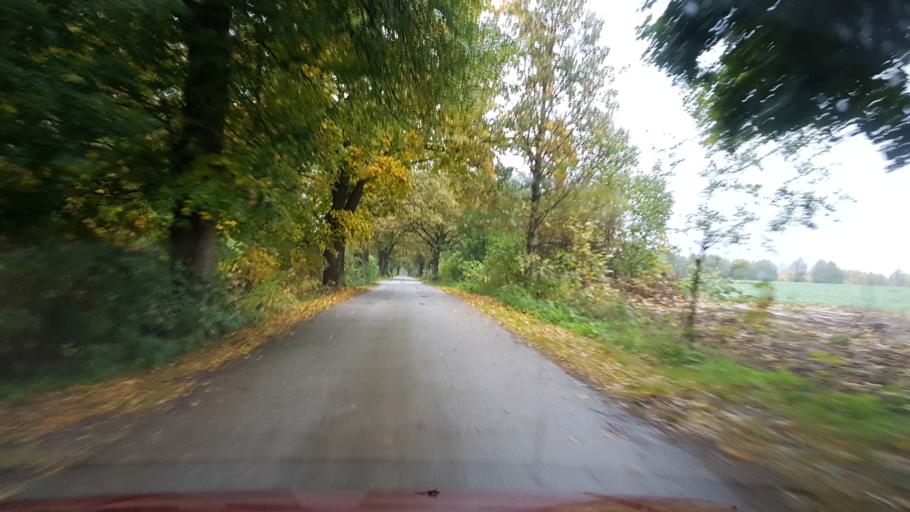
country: PL
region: West Pomeranian Voivodeship
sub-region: Koszalin
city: Koszalin
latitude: 54.1402
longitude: 16.1614
